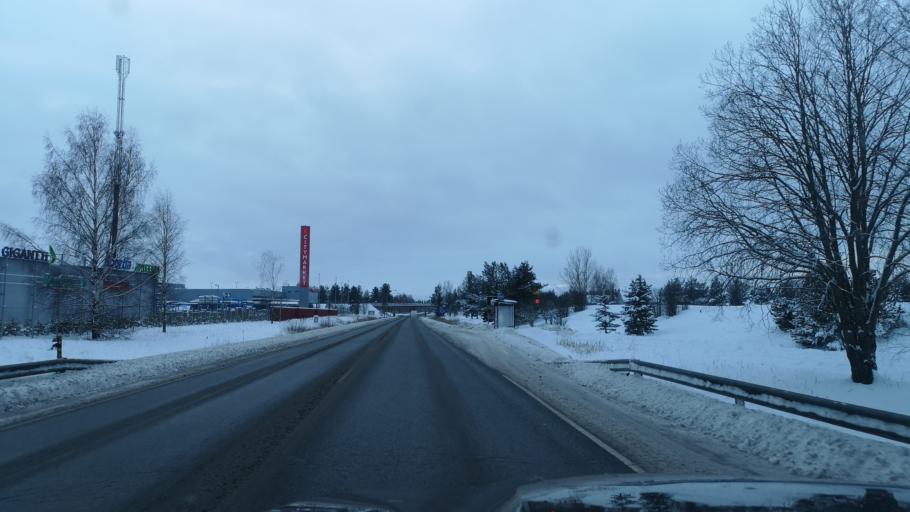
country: FI
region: Varsinais-Suomi
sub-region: Loimaa
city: Loimaa
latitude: 60.8576
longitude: 23.0432
